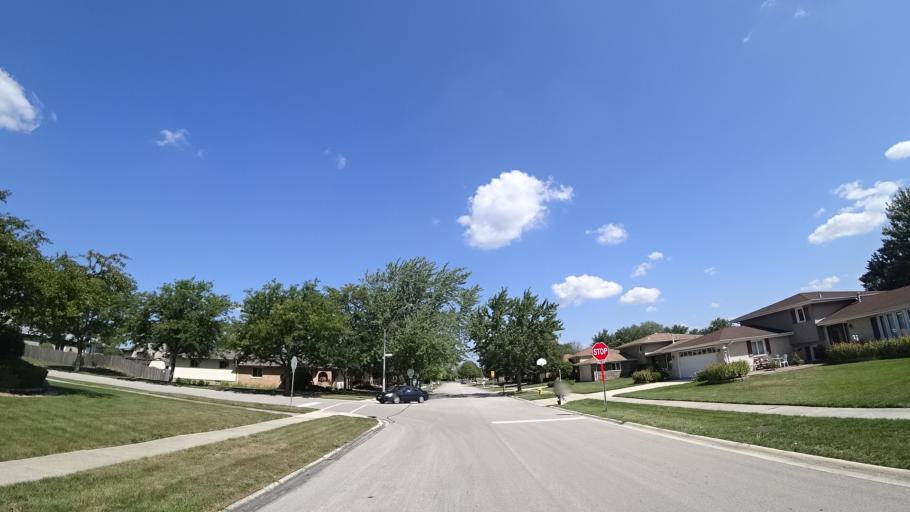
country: US
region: Illinois
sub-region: Cook County
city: Orland Park
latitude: 41.6324
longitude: -87.8440
